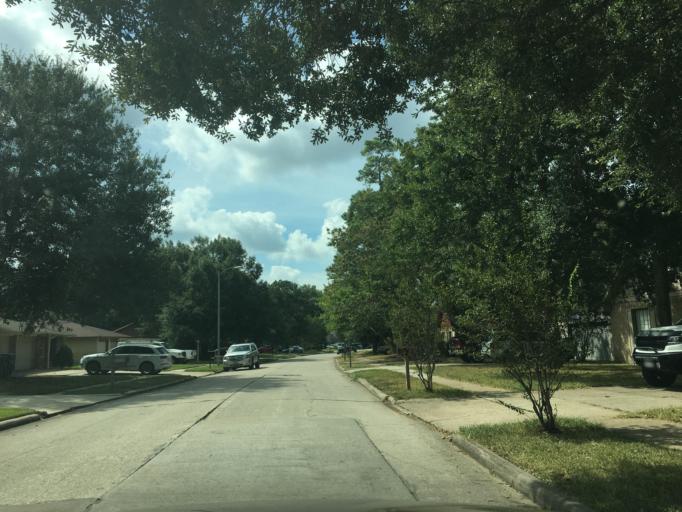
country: US
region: Texas
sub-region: Harris County
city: Spring
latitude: 30.1170
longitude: -95.4010
